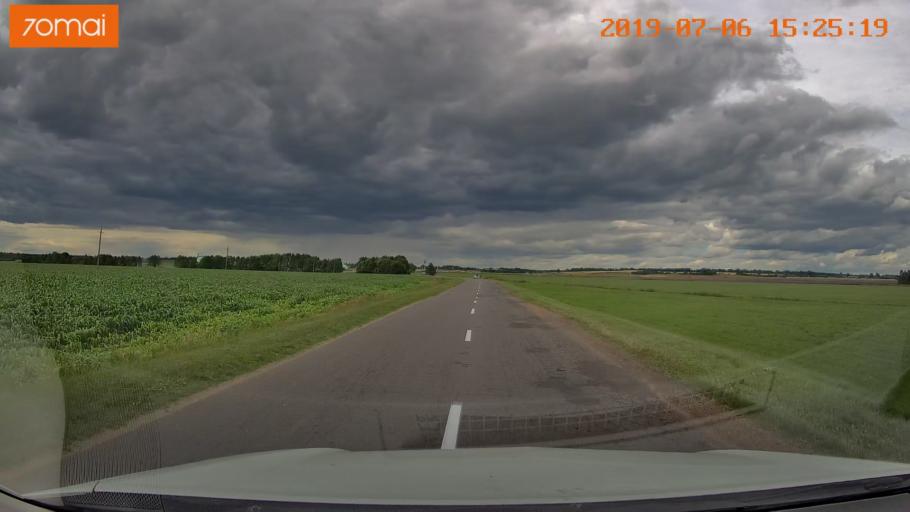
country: BY
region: Minsk
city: Valozhyn
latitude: 54.0302
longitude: 26.6040
